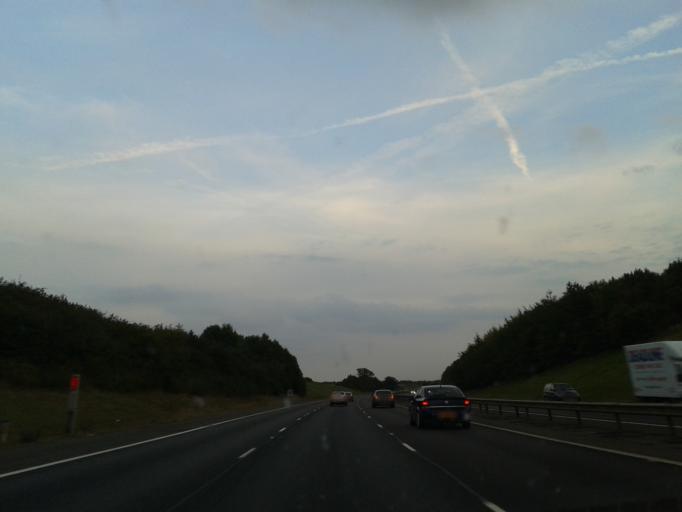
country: GB
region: England
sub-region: Warwickshire
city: Warwick
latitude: 52.2535
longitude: -1.5771
